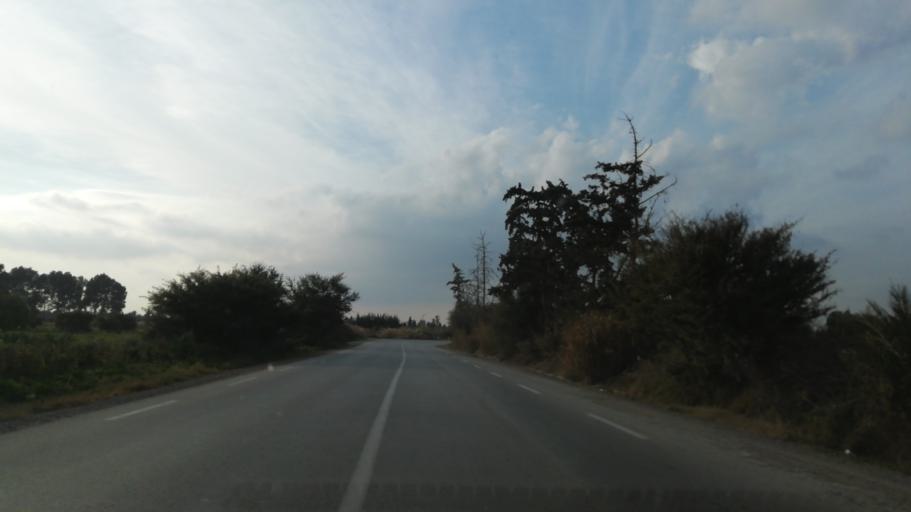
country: DZ
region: Mascara
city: Mascara
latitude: 35.6174
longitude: 0.0501
